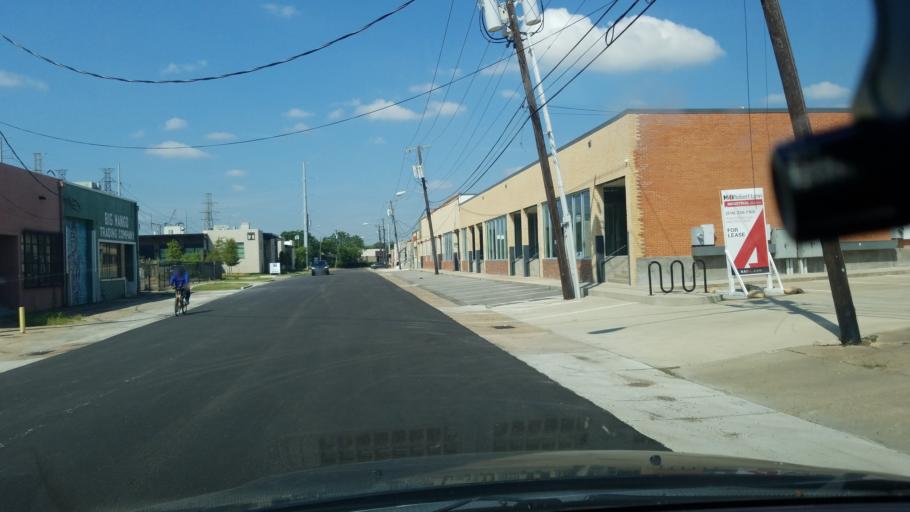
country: US
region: Texas
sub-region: Dallas County
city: Dallas
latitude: 32.7857
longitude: -96.8186
